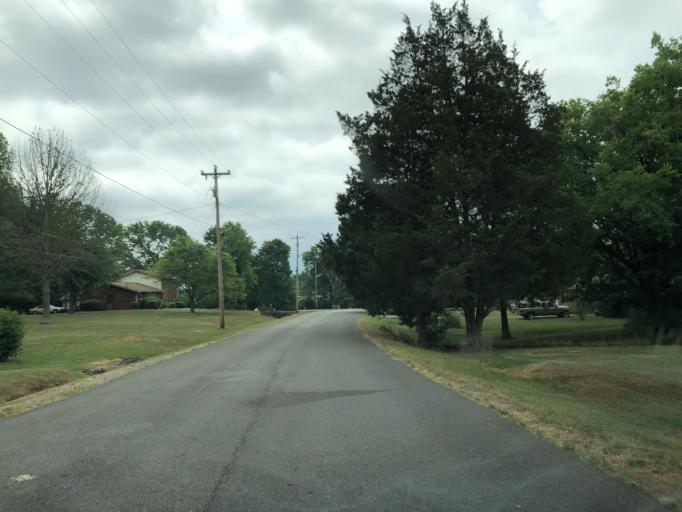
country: US
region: Tennessee
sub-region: Davidson County
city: Goodlettsville
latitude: 36.2894
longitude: -86.7285
